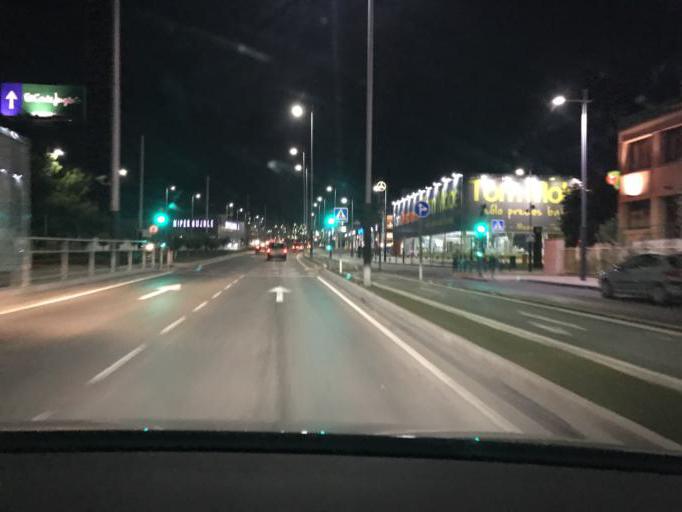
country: ES
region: Andalusia
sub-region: Provincia de Jaen
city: Jaen
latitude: 37.7955
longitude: -3.7798
